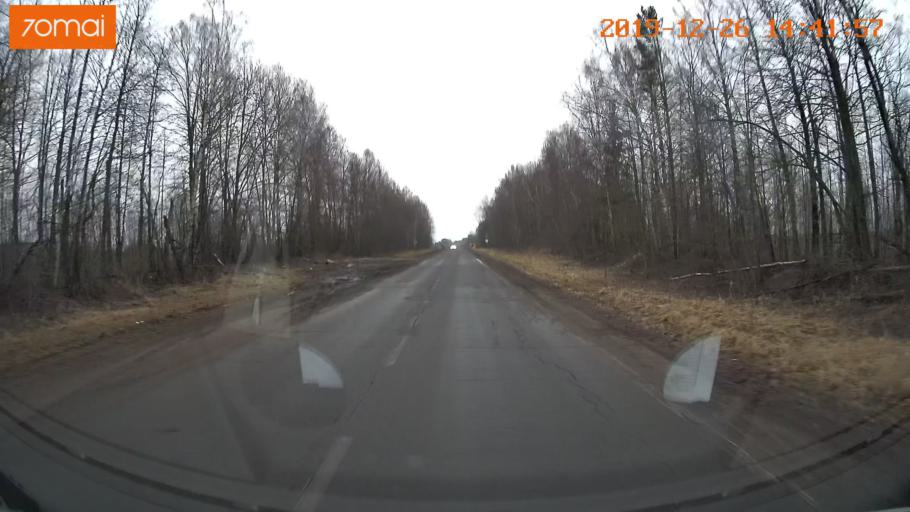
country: RU
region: Jaroslavl
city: Poshekhon'ye
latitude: 58.3673
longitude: 39.0253
